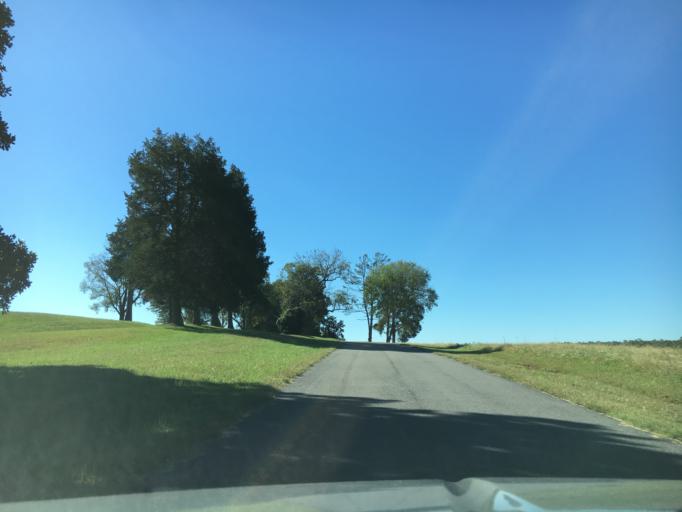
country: US
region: Virginia
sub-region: Goochland County
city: Goochland
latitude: 37.6977
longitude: -77.8325
